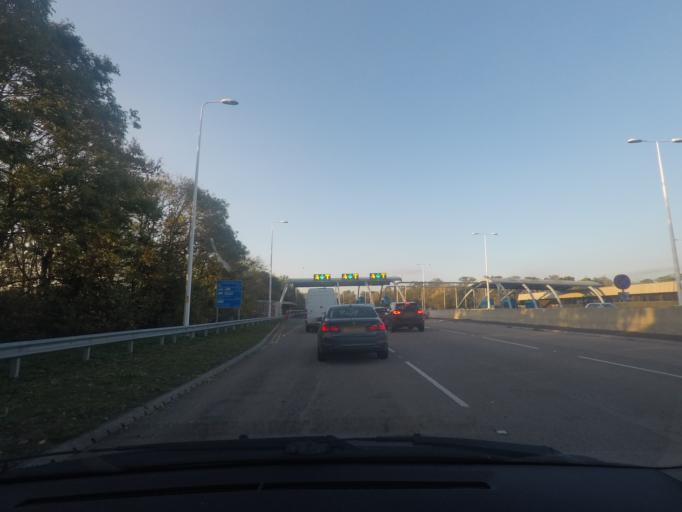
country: GB
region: England
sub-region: East Riding of Yorkshire
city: Hessle
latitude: 53.7193
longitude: -0.4516
